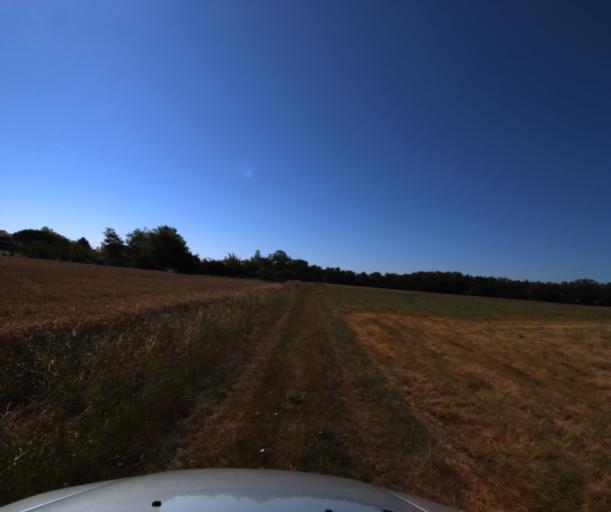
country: FR
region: Midi-Pyrenees
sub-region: Departement de la Haute-Garonne
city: Eaunes
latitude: 43.4126
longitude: 1.3588
